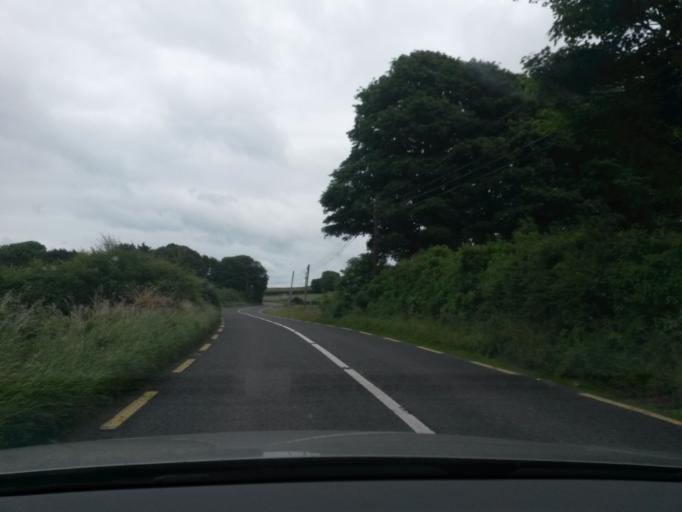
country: IE
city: Ballisodare
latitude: 54.2067
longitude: -8.5478
